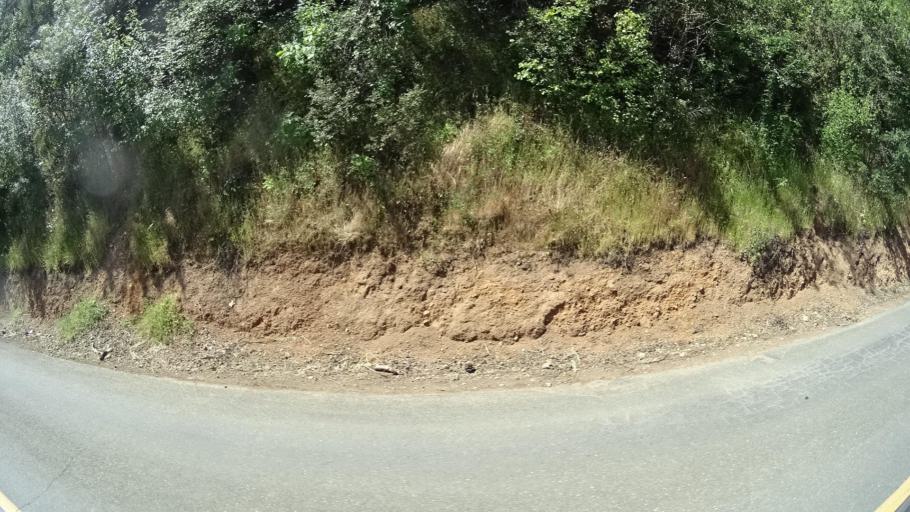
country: US
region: California
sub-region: Lake County
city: Clearlake
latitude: 38.9471
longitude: -122.6867
